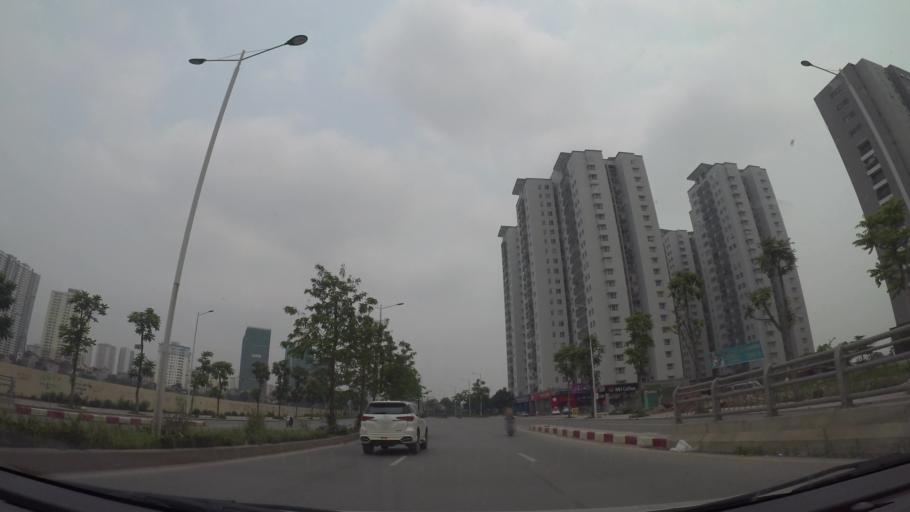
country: VN
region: Ha Noi
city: Cau Dien
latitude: 21.0324
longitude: 105.7548
